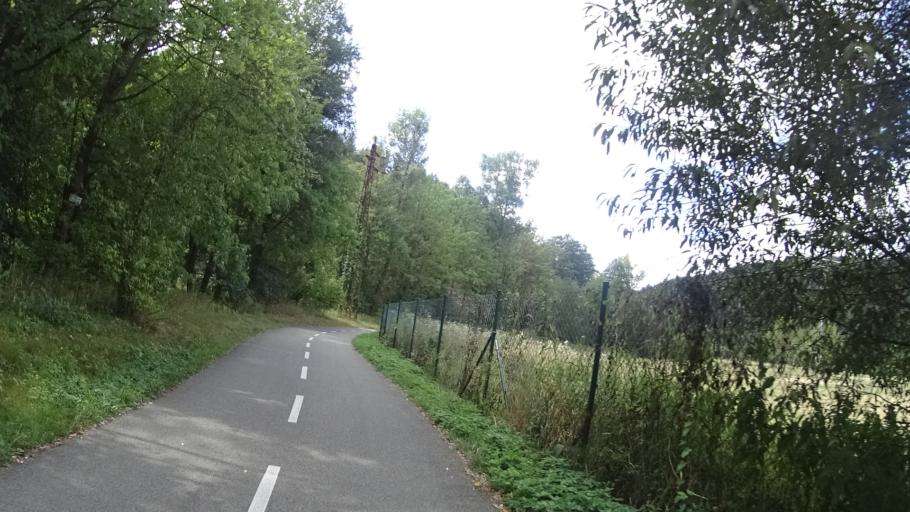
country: CZ
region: Pardubicky
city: Dolni Dobrouc
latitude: 50.0001
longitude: 16.4574
